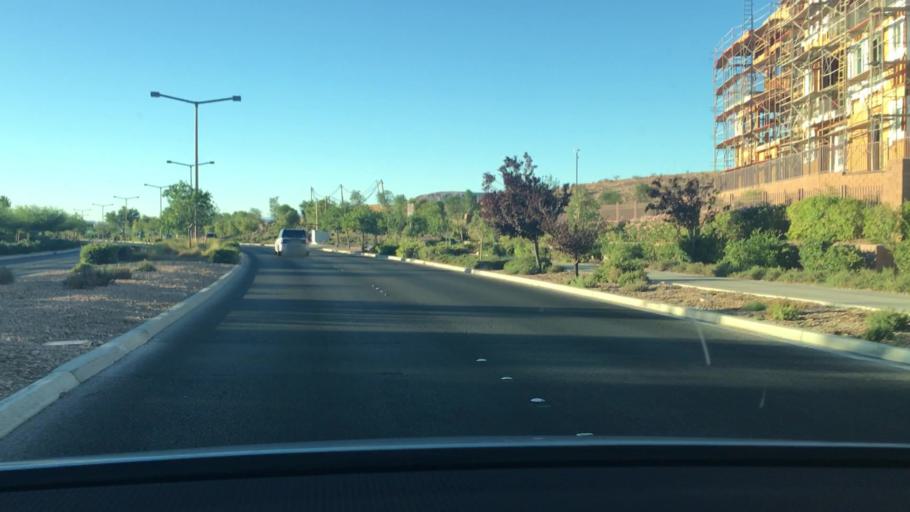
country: US
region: Nevada
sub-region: Clark County
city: Summerlin South
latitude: 36.1113
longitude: -115.3298
